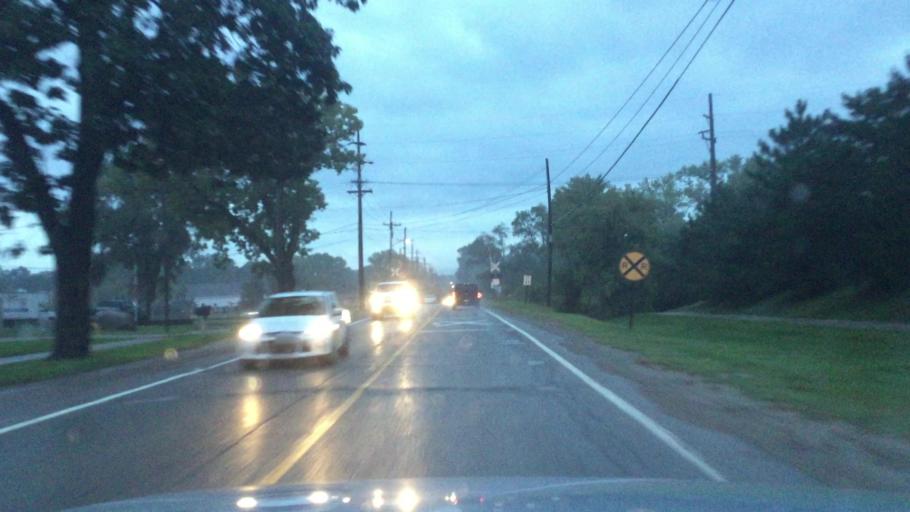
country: US
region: Michigan
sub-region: Oakland County
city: Waterford
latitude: 42.6934
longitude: -83.4075
